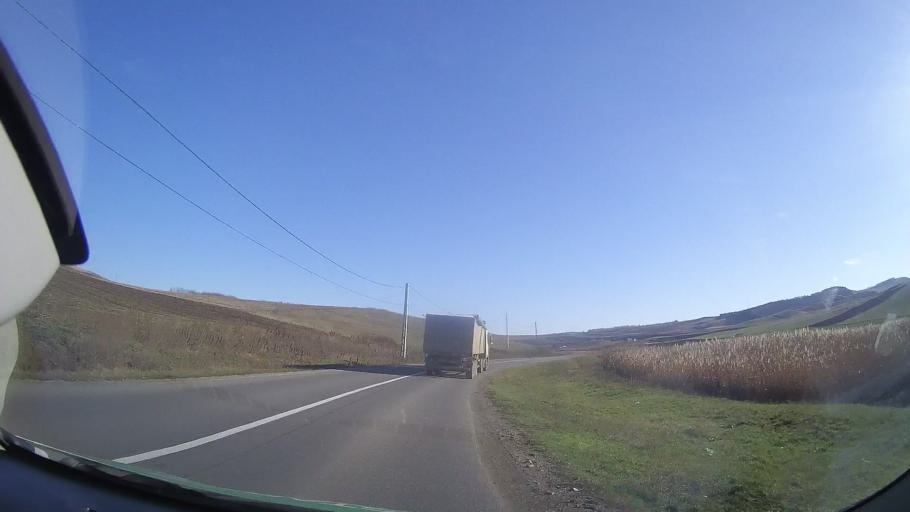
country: RO
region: Mures
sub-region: Comuna Mihesu de Campie
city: Mihesu de Campie
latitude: 46.6493
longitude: 24.1504
